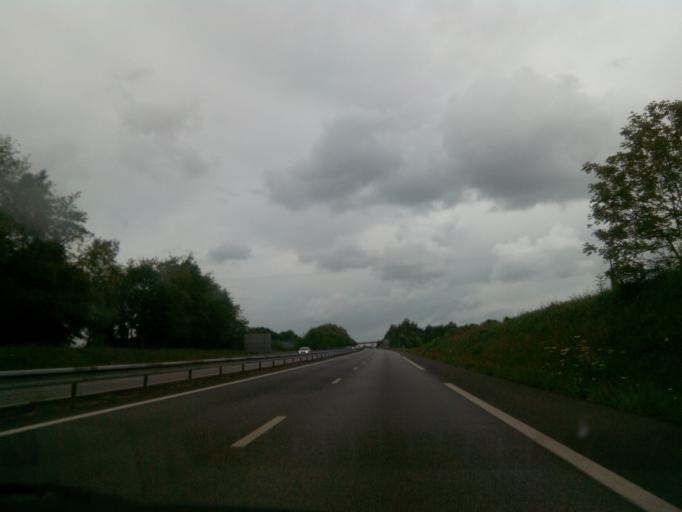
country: FR
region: Brittany
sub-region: Departement du Morbihan
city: Ploermel
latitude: 47.8784
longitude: -2.4170
